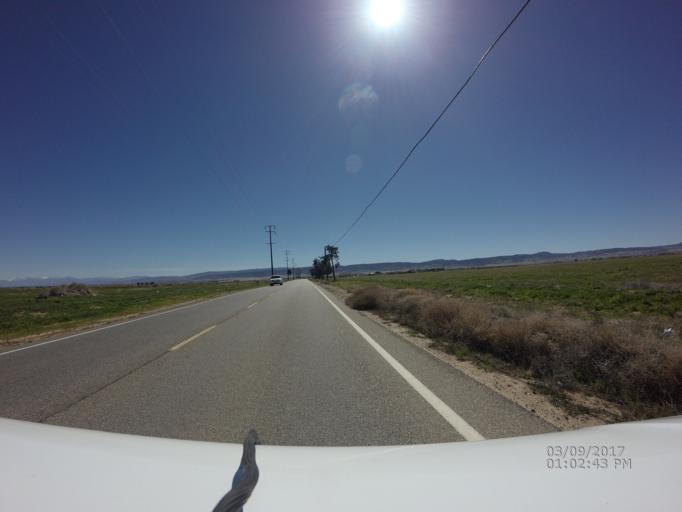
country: US
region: California
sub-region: Los Angeles County
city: Quartz Hill
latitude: 34.7394
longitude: -118.2902
